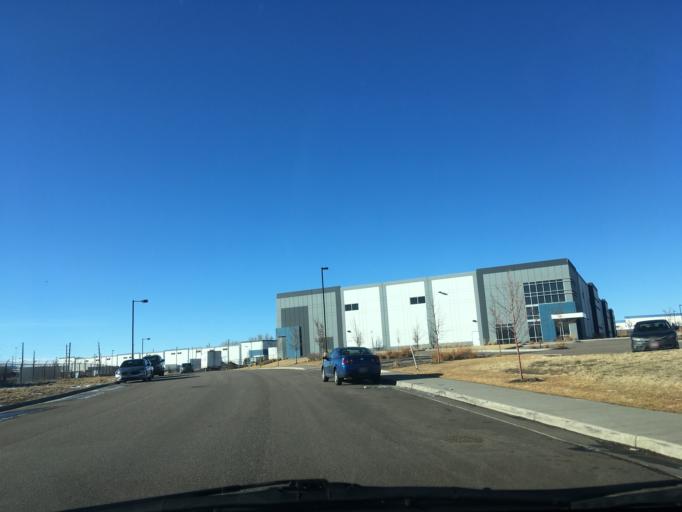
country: US
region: Colorado
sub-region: Adams County
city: Twin Lakes
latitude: 39.7939
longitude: -104.9824
